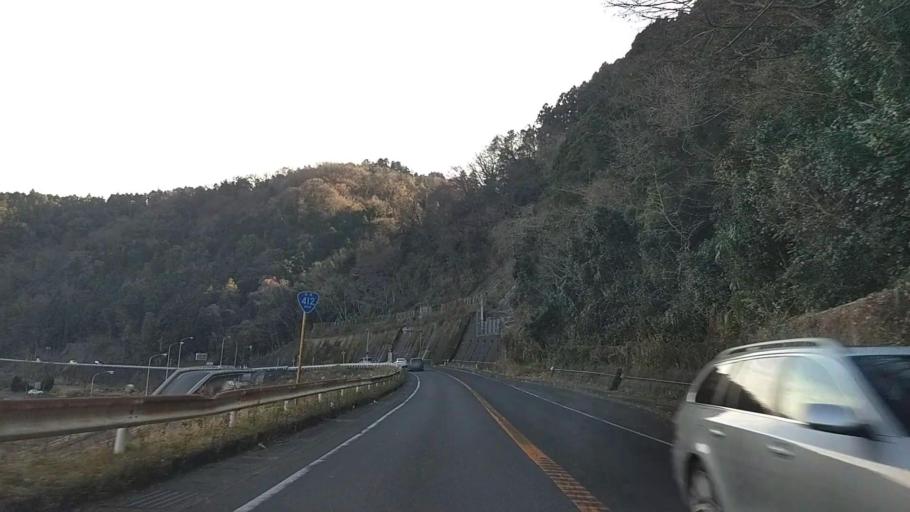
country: JP
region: Kanagawa
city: Zama
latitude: 35.5260
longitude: 139.2810
